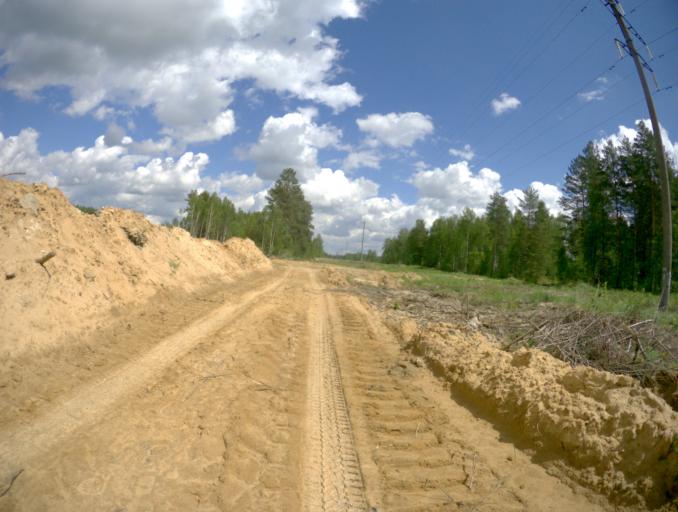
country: RU
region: Vladimir
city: Velikodvorskiy
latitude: 55.2259
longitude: 40.6361
